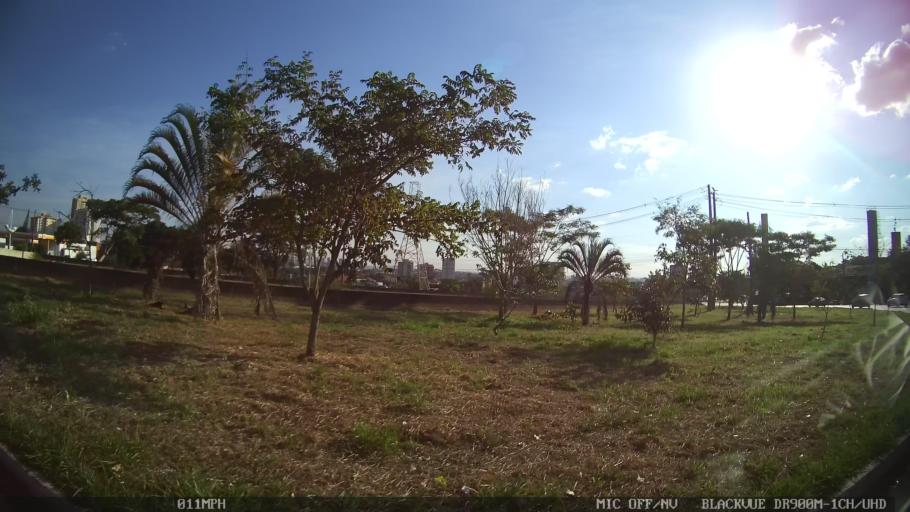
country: BR
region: Sao Paulo
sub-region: Ribeirao Preto
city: Ribeirao Preto
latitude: -21.1935
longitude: -47.7756
